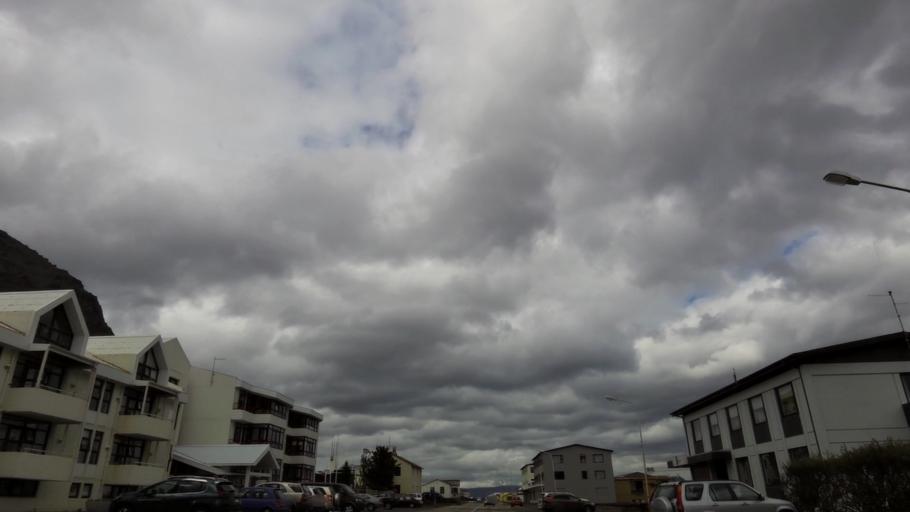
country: IS
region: Westfjords
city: Isafjoerdur
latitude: 66.1578
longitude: -23.2495
